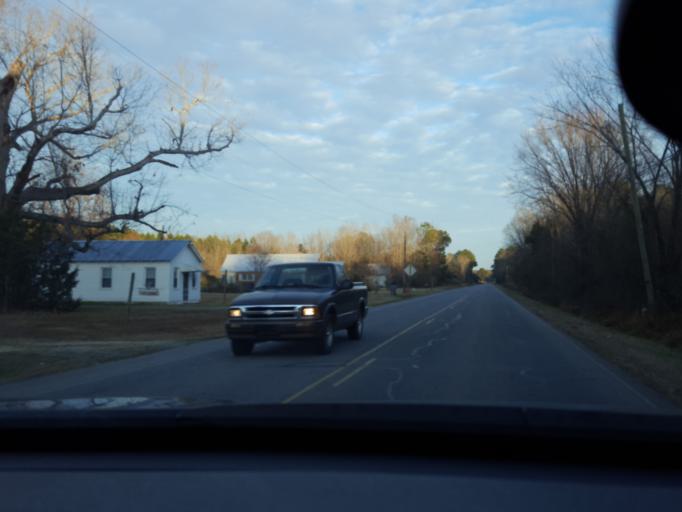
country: US
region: North Carolina
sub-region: Northampton County
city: Jackson
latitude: 36.2695
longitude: -77.2617
